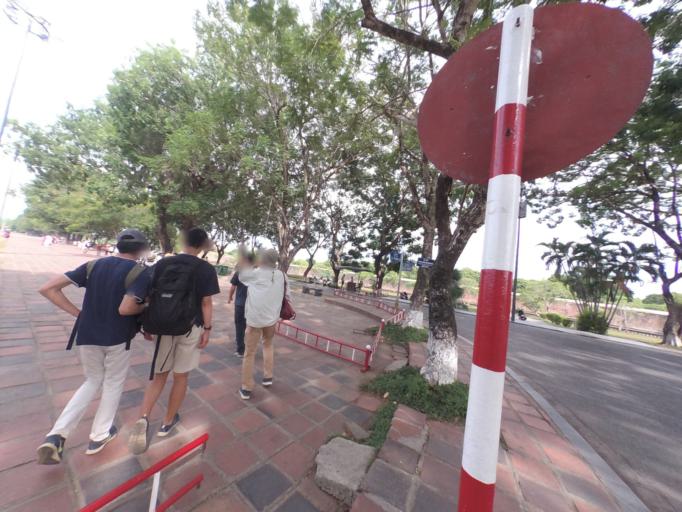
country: VN
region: Thua Thien-Hue
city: Hue
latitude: 16.4681
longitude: 107.5809
